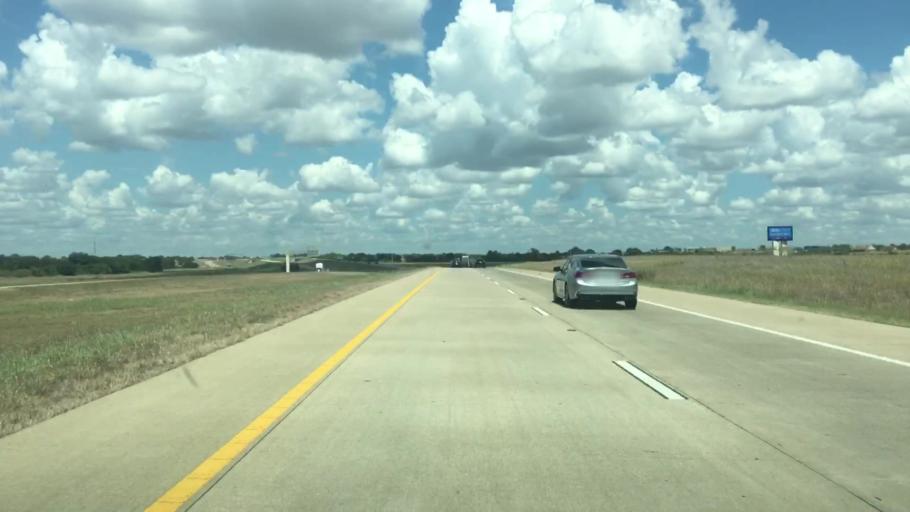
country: US
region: Texas
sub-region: Williamson County
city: Hutto
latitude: 30.5523
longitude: -97.5765
